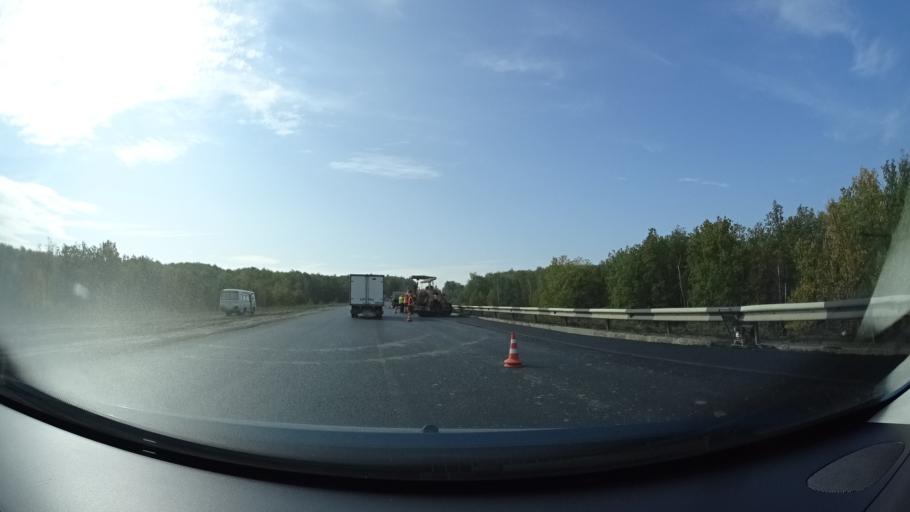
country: RU
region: Bashkortostan
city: Kandry
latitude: 54.5945
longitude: 54.2815
